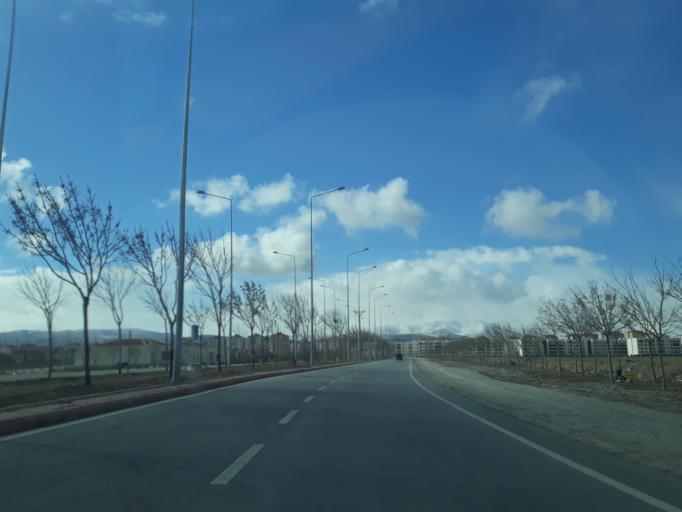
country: TR
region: Konya
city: Asagipinarbasi
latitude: 38.0055
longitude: 32.5461
